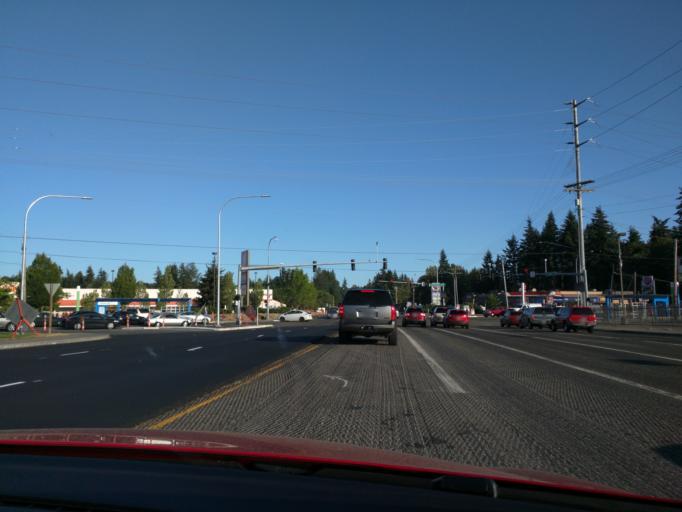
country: US
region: Washington
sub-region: Snohomish County
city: Martha Lake
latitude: 47.8900
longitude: -122.2589
